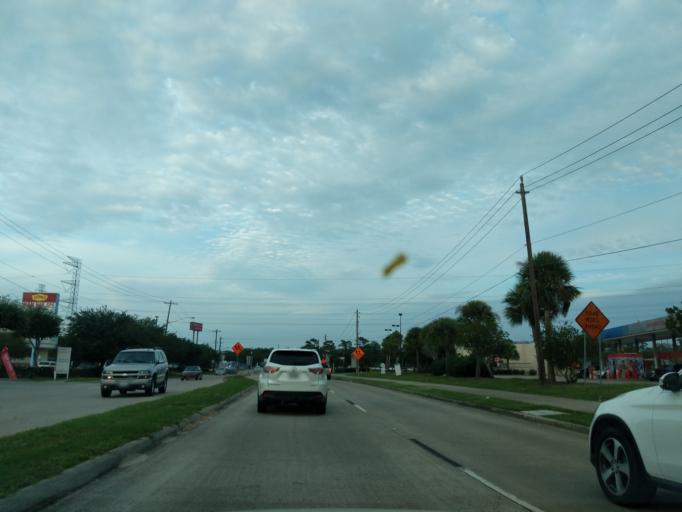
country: US
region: Texas
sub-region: Galveston County
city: Kemah
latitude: 29.5365
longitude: -95.0202
